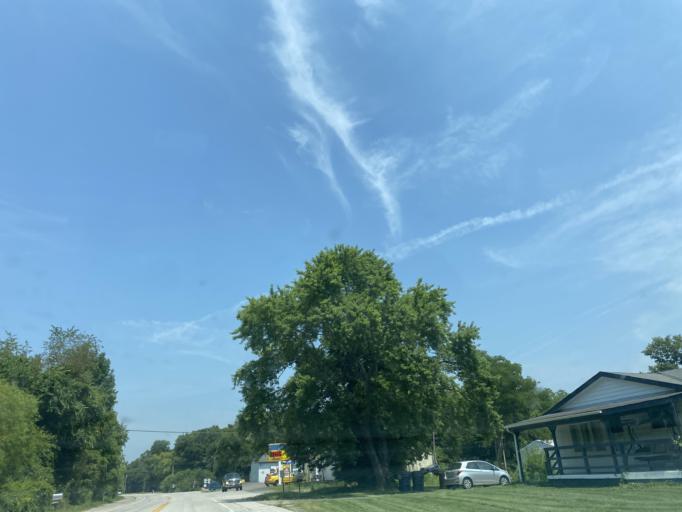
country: US
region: Kentucky
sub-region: Kenton County
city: Ryland Heights
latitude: 38.9181
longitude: -84.4524
